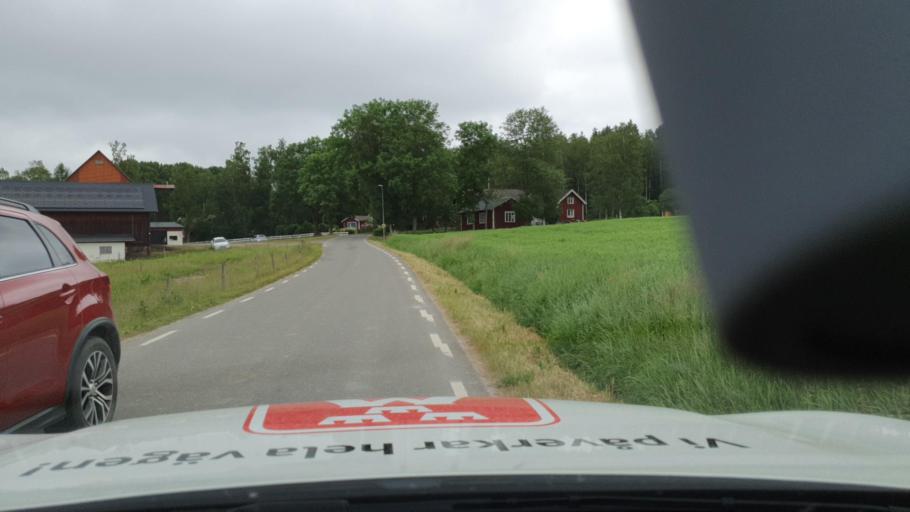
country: SE
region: Vaestra Goetaland
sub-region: Tibro Kommun
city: Tibro
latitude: 58.3845
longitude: 14.1849
